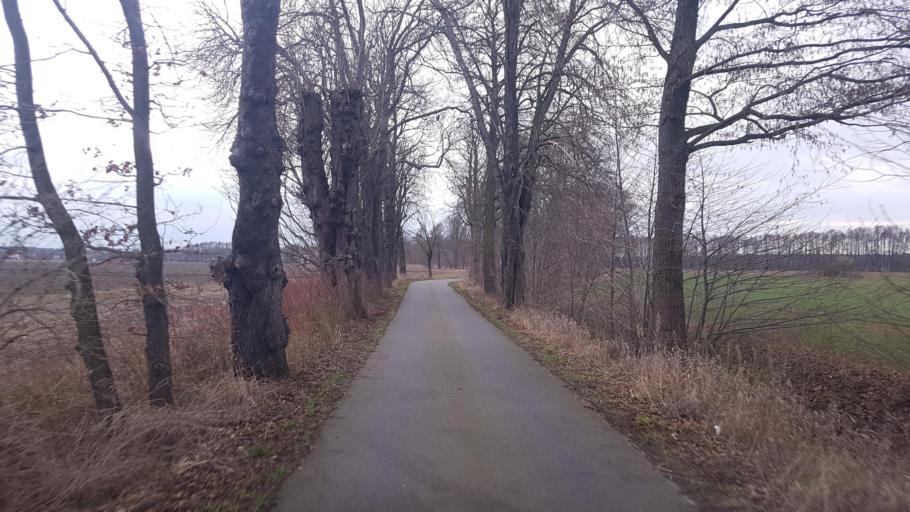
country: DE
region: Brandenburg
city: Drahnsdorf
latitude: 51.9309
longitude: 13.6054
